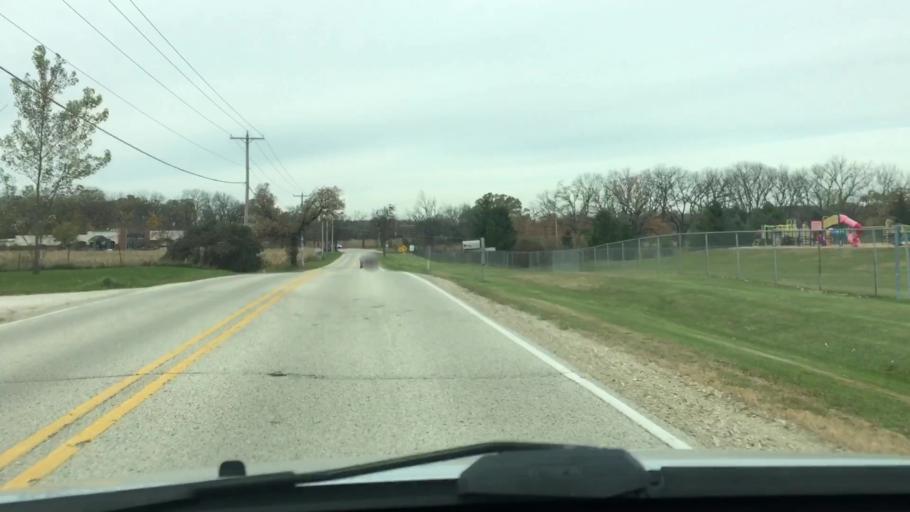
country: US
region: Wisconsin
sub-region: Waukesha County
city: North Prairie
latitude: 42.8915
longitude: -88.3824
